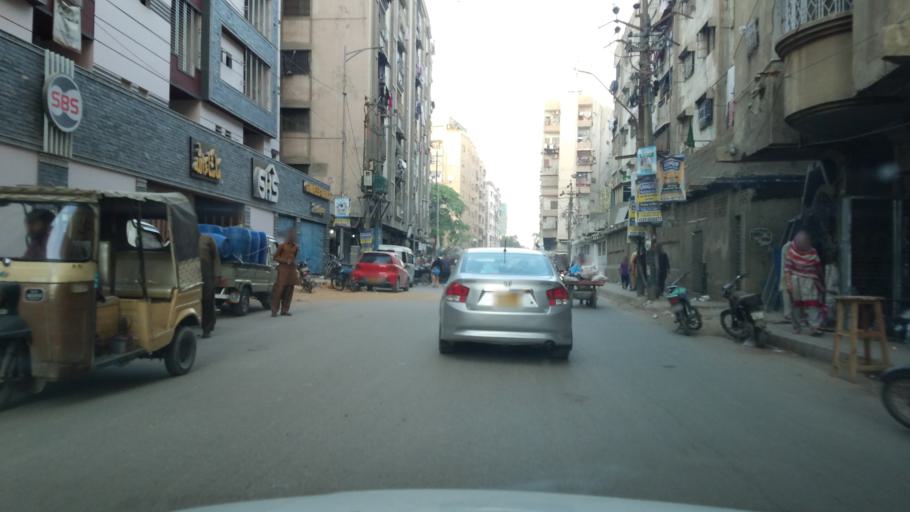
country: PK
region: Sindh
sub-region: Karachi District
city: Karachi
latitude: 24.8781
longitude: 67.0198
